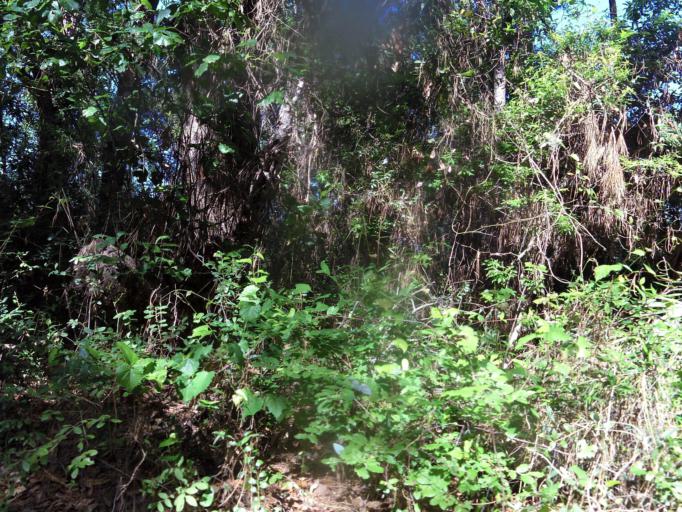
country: US
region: Florida
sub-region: Duval County
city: Atlantic Beach
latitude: 30.4604
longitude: -81.4865
